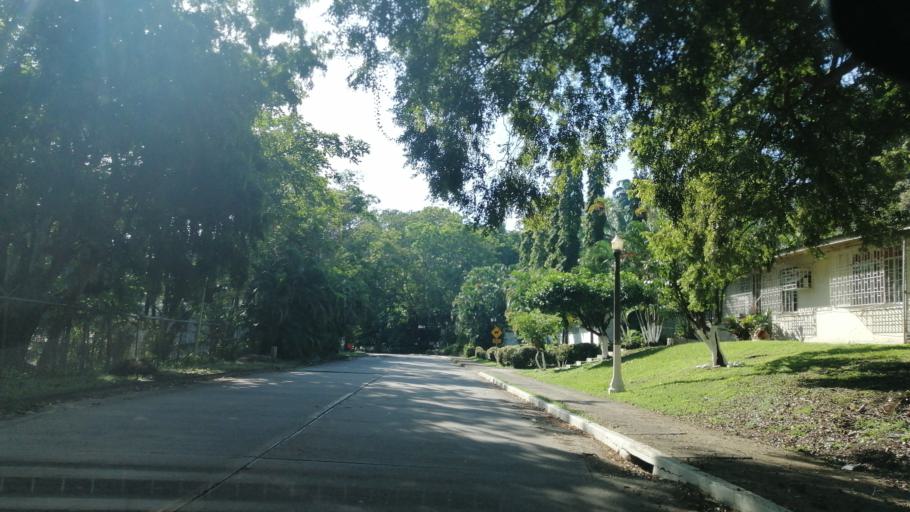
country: PA
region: Panama
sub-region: Distrito de Panama
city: Ancon
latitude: 8.9636
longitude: -79.5479
